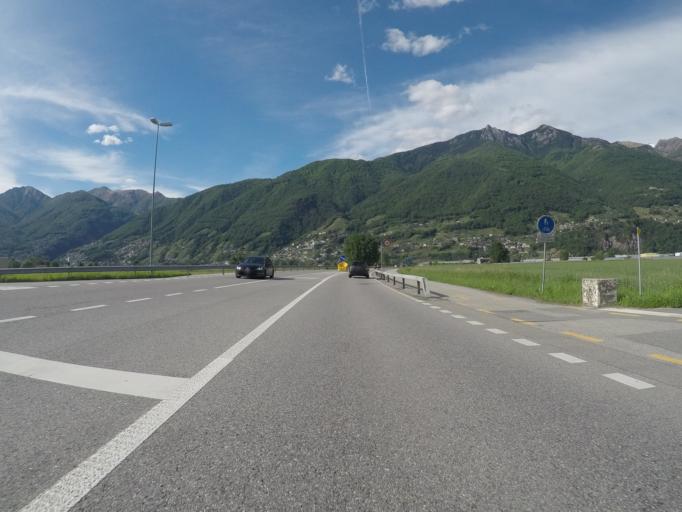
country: CH
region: Ticino
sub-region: Locarno District
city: Gordola
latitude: 46.1643
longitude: 8.8860
